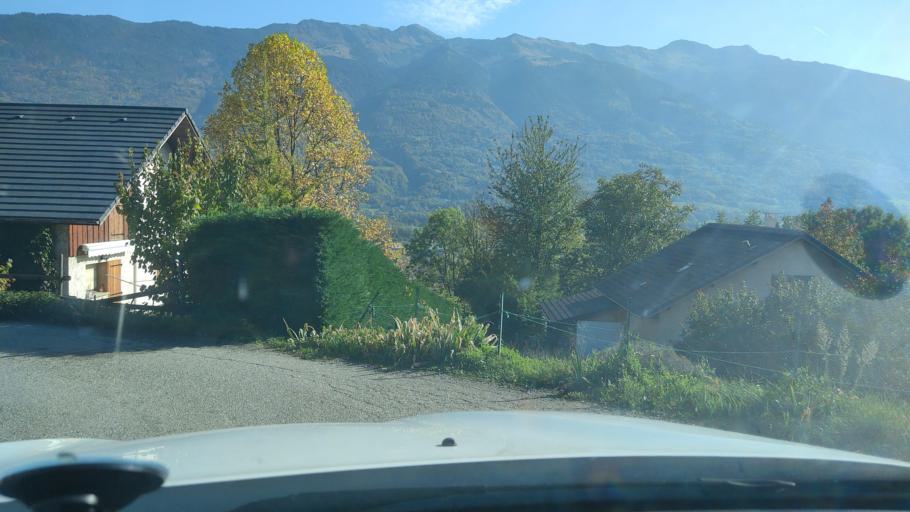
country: FR
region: Rhone-Alpes
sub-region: Departement de la Savoie
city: Frontenex
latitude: 45.6412
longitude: 6.3200
